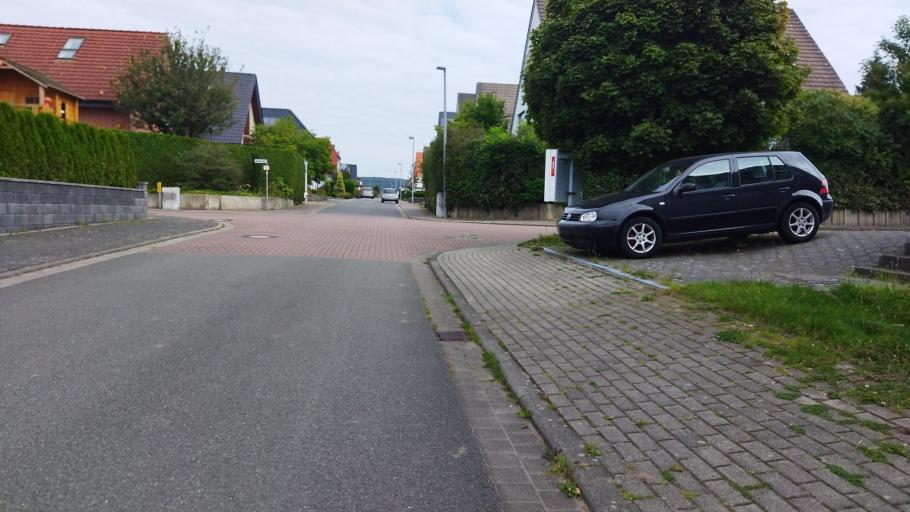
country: DE
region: Lower Saxony
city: Hilter
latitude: 52.1297
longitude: 8.1471
